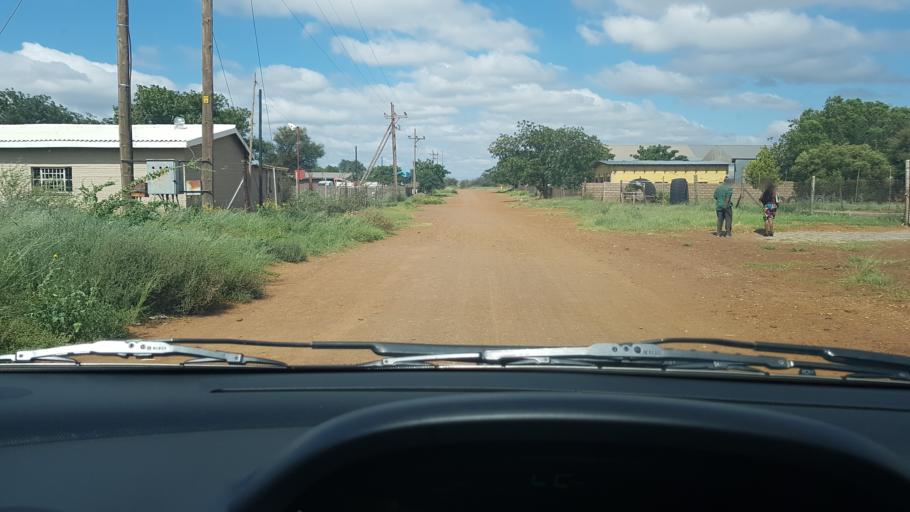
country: ZA
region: Northern Cape
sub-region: Siyanda District Municipality
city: Danielskuil
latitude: -28.1913
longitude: 23.5432
